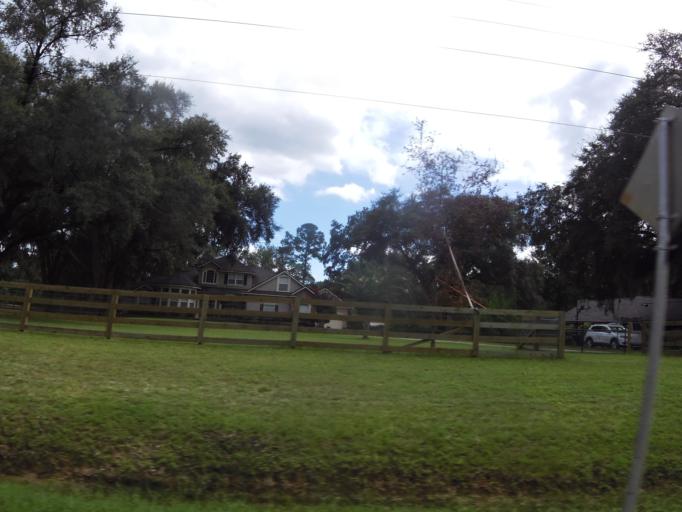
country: US
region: Florida
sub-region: Clay County
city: Asbury Lake
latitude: 30.0766
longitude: -81.8014
